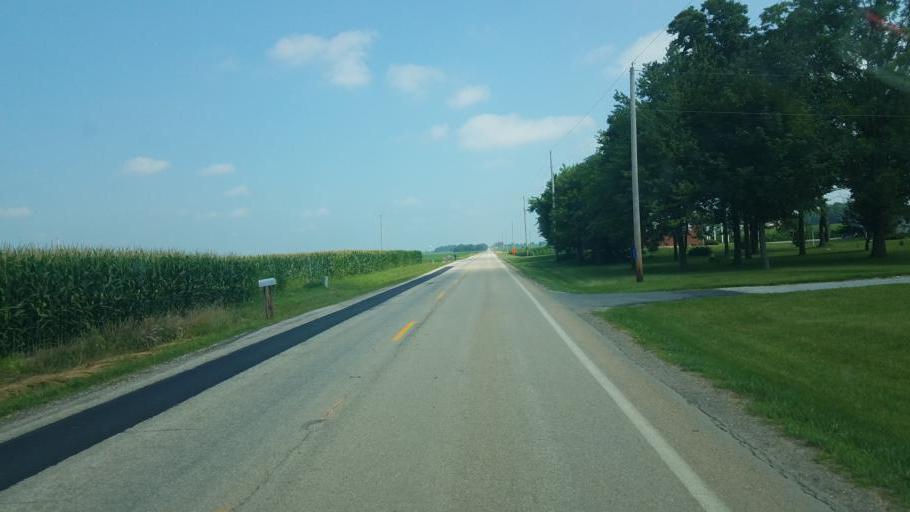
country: US
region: Ohio
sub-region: Crawford County
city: Bucyrus
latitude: 40.9286
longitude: -82.8542
